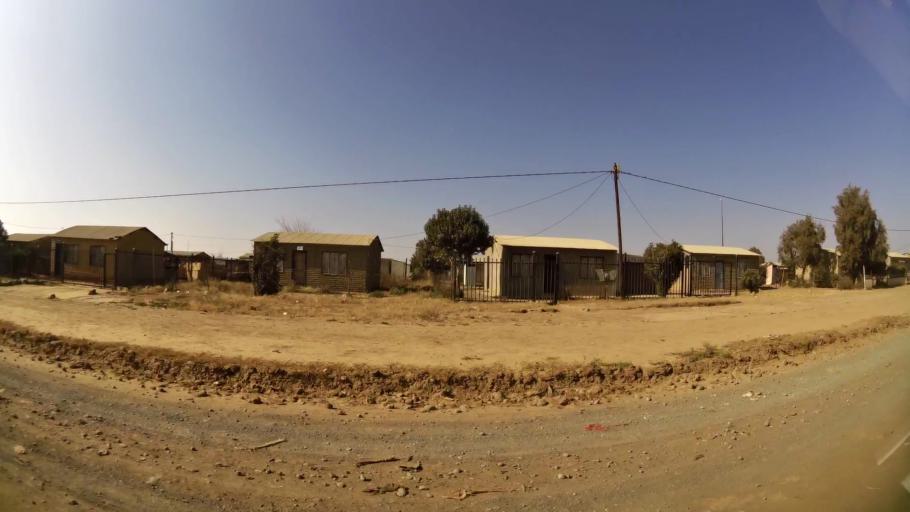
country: ZA
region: Orange Free State
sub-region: Mangaung Metropolitan Municipality
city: Bloemfontein
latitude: -29.1799
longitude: 26.2873
